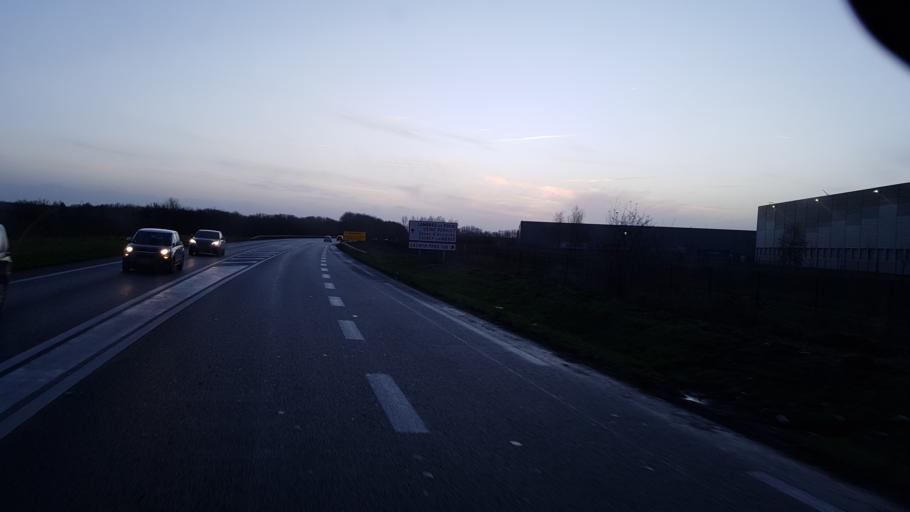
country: FR
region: Nord-Pas-de-Calais
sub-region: Departement du Nord
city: Lauwin-Planque
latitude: 50.3951
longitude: 3.0388
